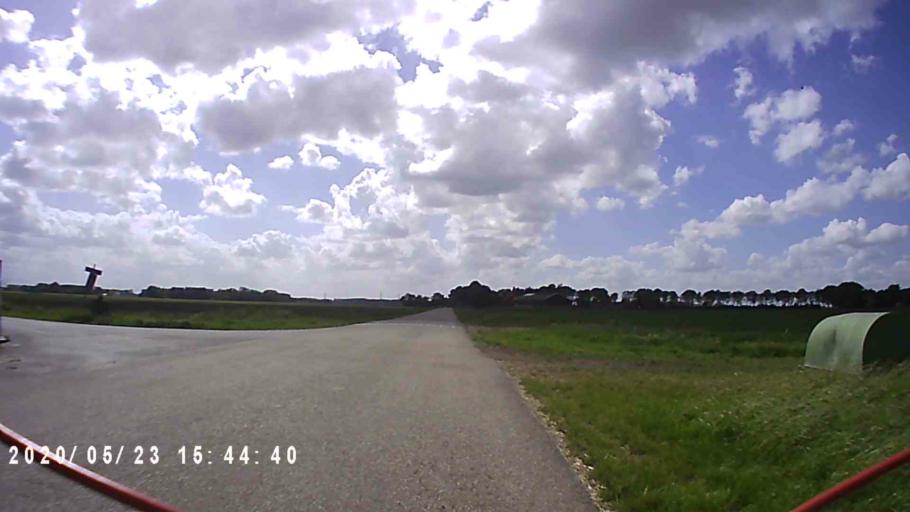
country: NL
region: Groningen
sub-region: Gemeente Delfzijl
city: Delfzijl
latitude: 53.2798
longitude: 6.9169
